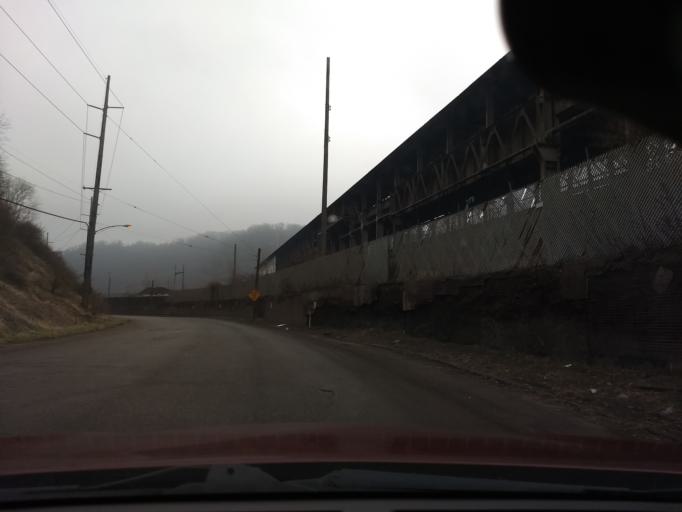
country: US
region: Pennsylvania
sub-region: Allegheny County
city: North Braddock
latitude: 40.3944
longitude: -79.8477
